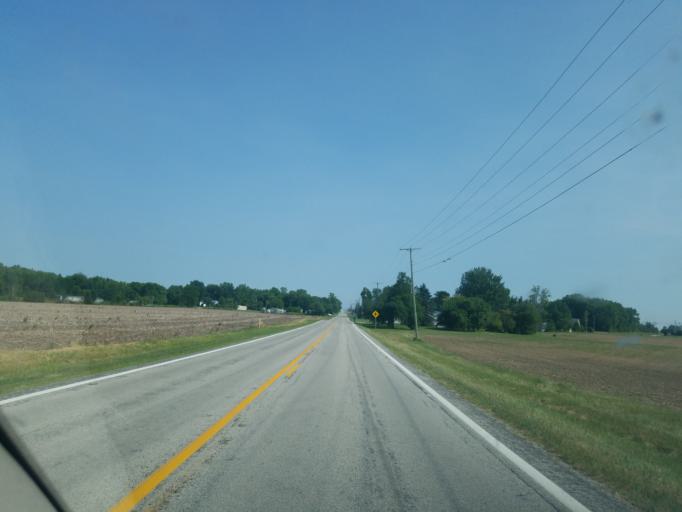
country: US
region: Ohio
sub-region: Wyandot County
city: Carey
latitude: 41.0319
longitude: -83.3009
